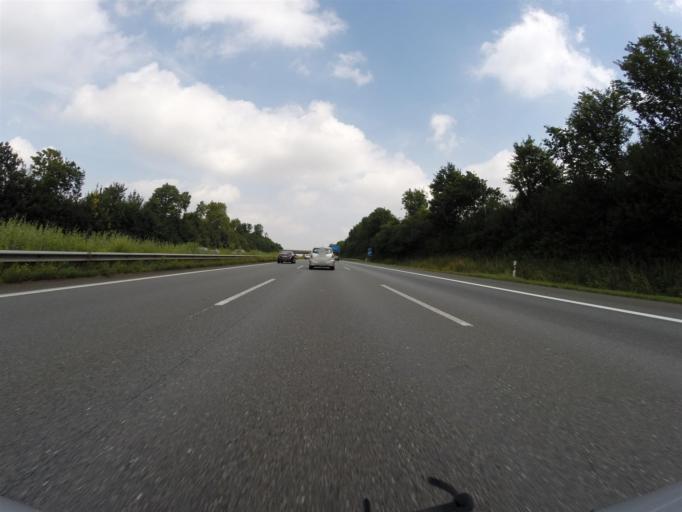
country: DE
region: North Rhine-Westphalia
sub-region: Regierungsbezirk Detmold
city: Leopoldshohe
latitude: 52.0549
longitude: 8.6582
